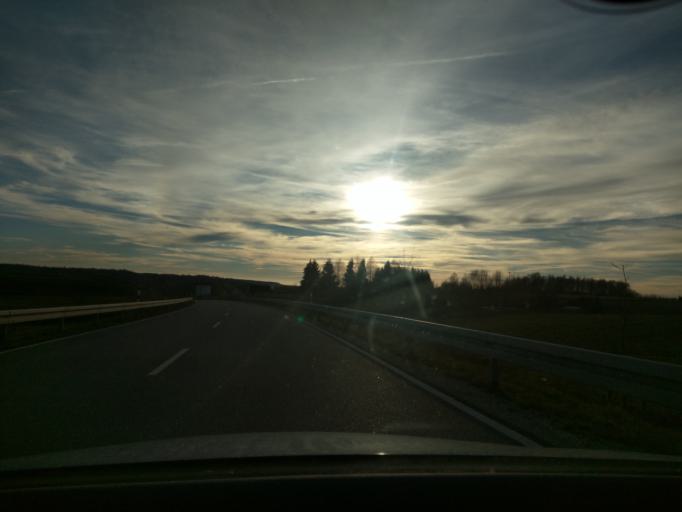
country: DE
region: Bavaria
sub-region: Upper Bavaria
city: Au in der Hallertau
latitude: 48.5612
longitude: 11.7287
